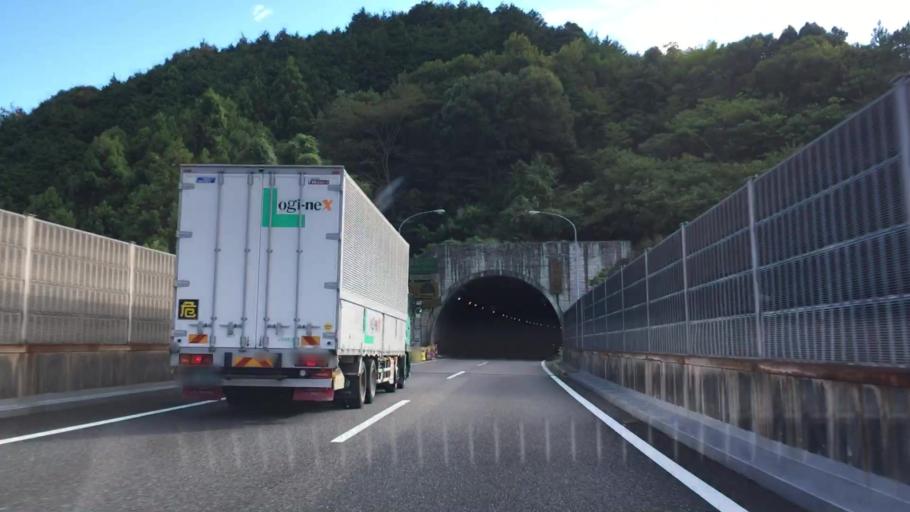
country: JP
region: Yamaguchi
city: Iwakuni
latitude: 34.1568
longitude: 132.1500
